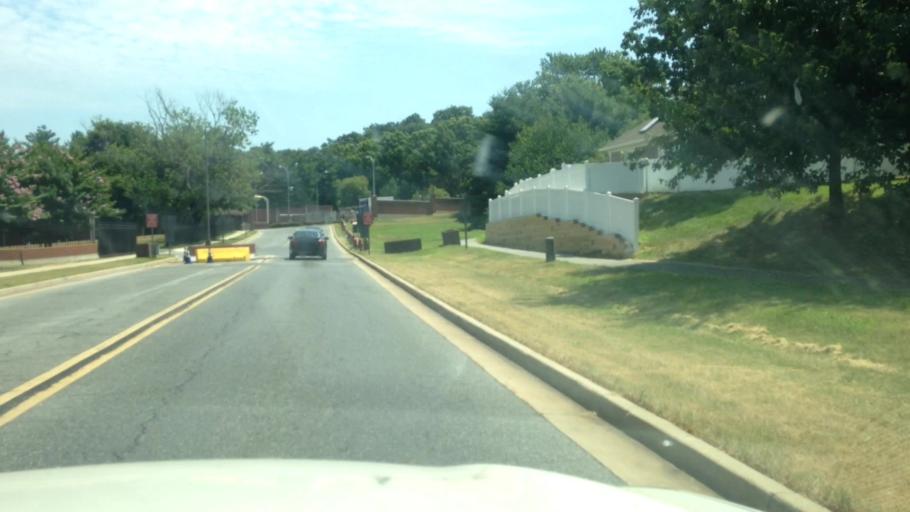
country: US
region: Maryland
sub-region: Prince George's County
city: Glassmanor
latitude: 38.8297
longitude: -77.0189
